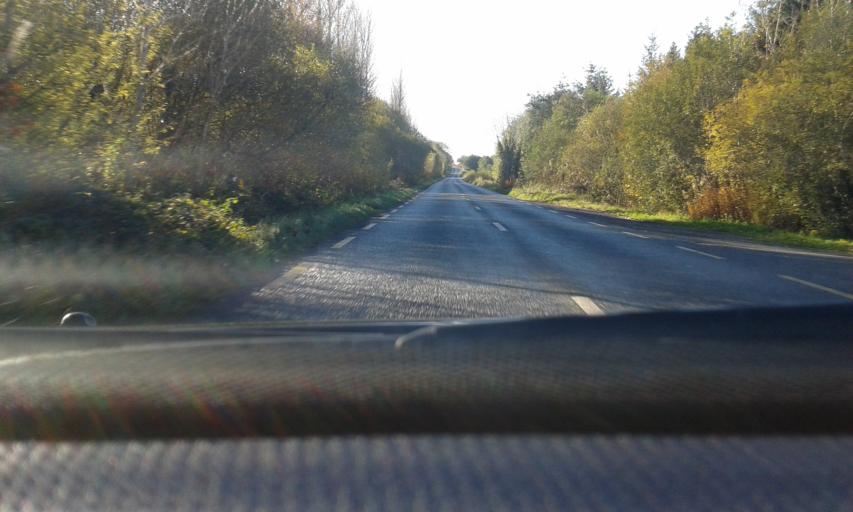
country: IE
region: Leinster
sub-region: Kildare
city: Rathangan
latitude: 53.1860
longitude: -7.0156
